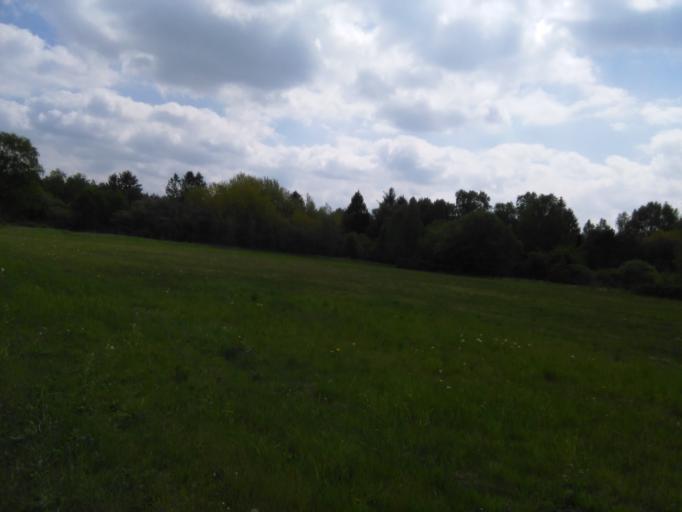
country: DK
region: Central Jutland
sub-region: Silkeborg Kommune
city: Svejbaek
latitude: 56.0521
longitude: 9.6739
